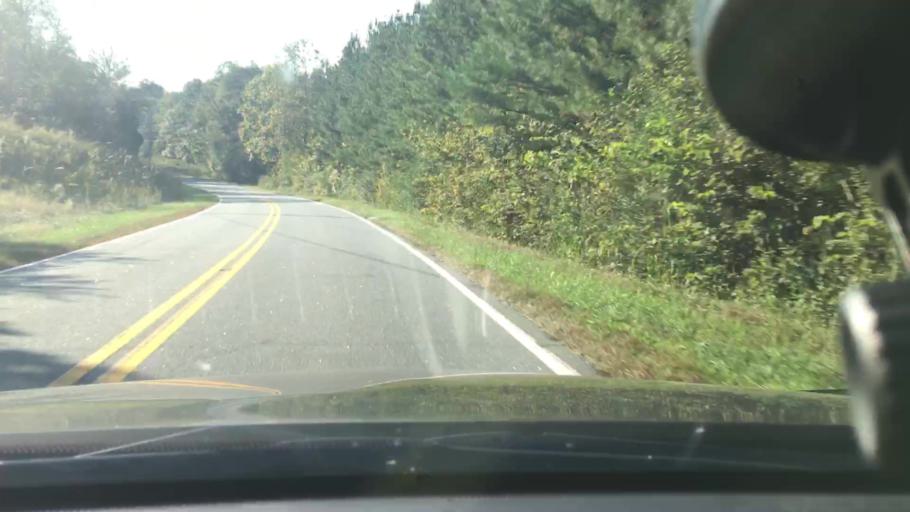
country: US
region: North Carolina
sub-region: Rutherford County
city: Rutherfordton
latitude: 35.3317
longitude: -82.0352
